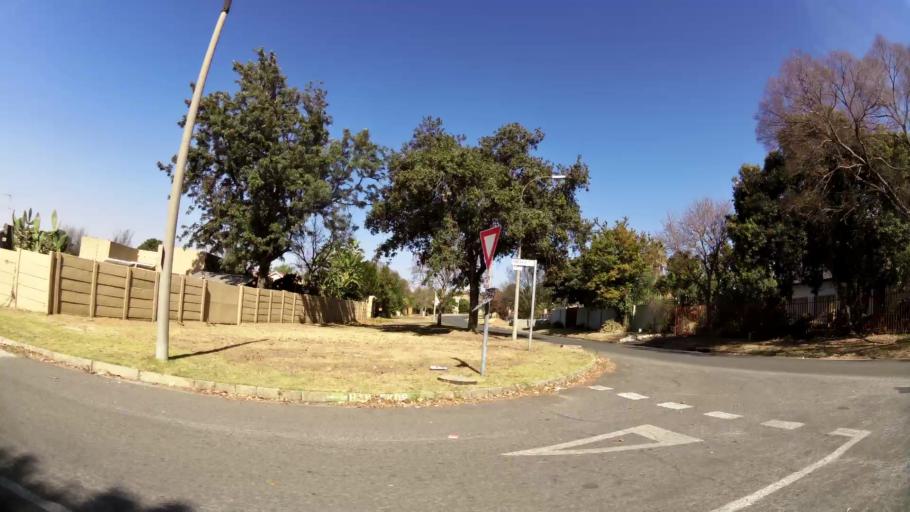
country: ZA
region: Gauteng
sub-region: City of Johannesburg Metropolitan Municipality
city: Modderfontein
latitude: -26.0546
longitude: 28.2093
